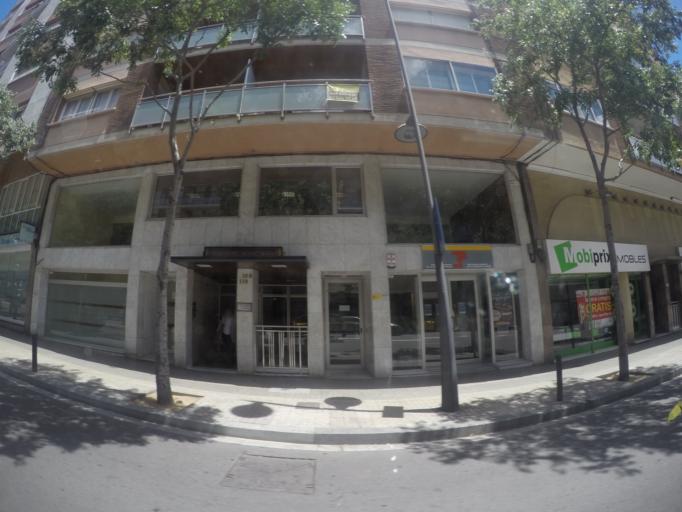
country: ES
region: Catalonia
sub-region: Provincia de Barcelona
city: Badalona
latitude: 41.4547
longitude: 2.2479
